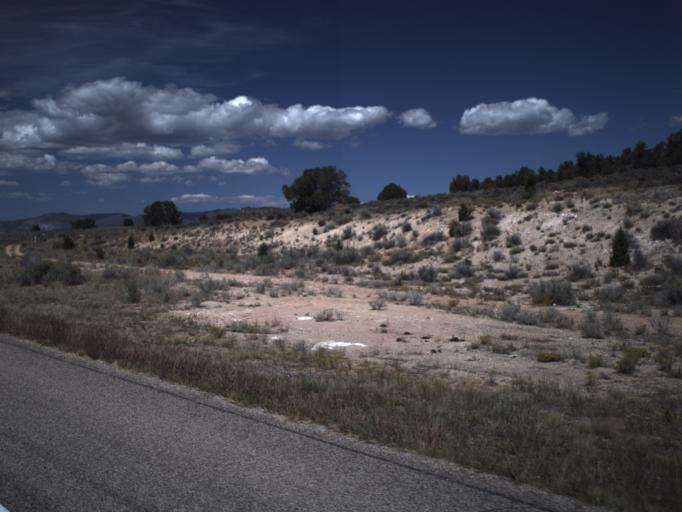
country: US
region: Utah
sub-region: Washington County
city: Ivins
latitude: 37.2753
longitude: -113.6474
